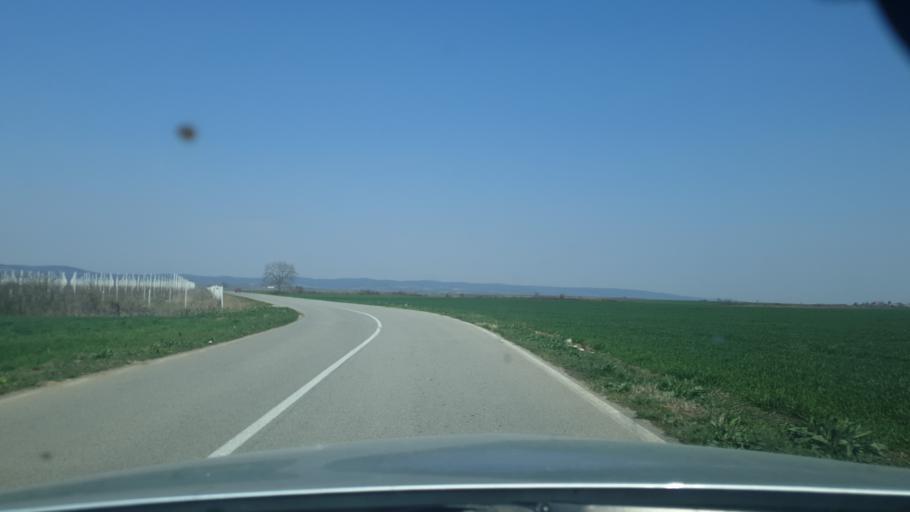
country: RS
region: Autonomna Pokrajina Vojvodina
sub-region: Sremski Okrug
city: Ruma
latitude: 45.0489
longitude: 19.7643
